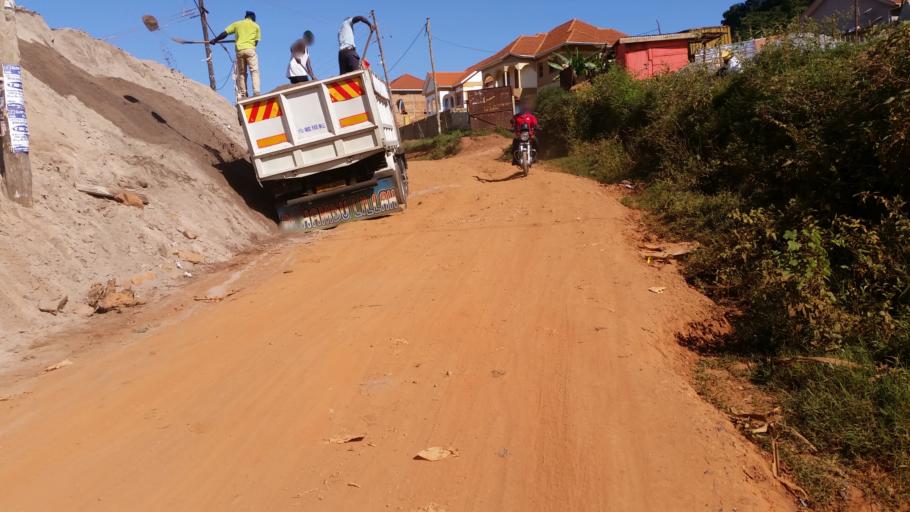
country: UG
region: Central Region
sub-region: Wakiso District
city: Kireka
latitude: 0.3433
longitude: 32.6523
